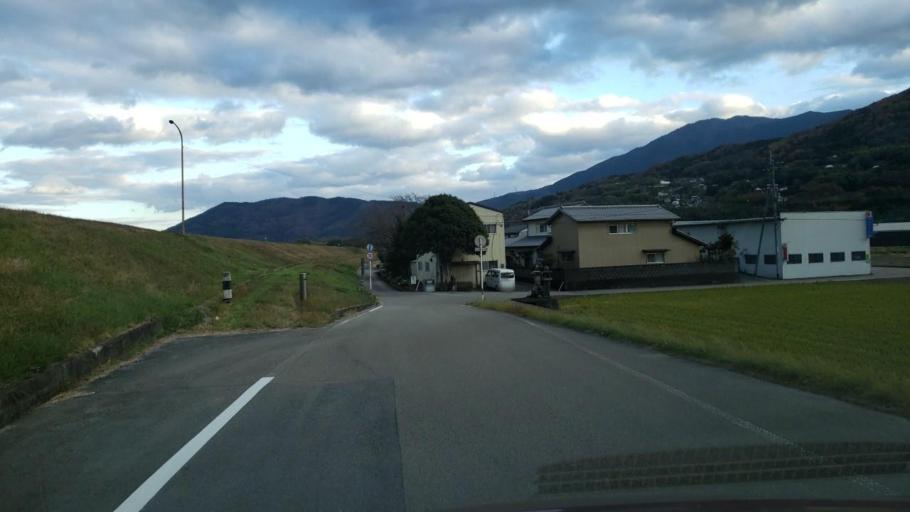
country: JP
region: Tokushima
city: Wakimachi
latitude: 34.0623
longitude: 134.1432
